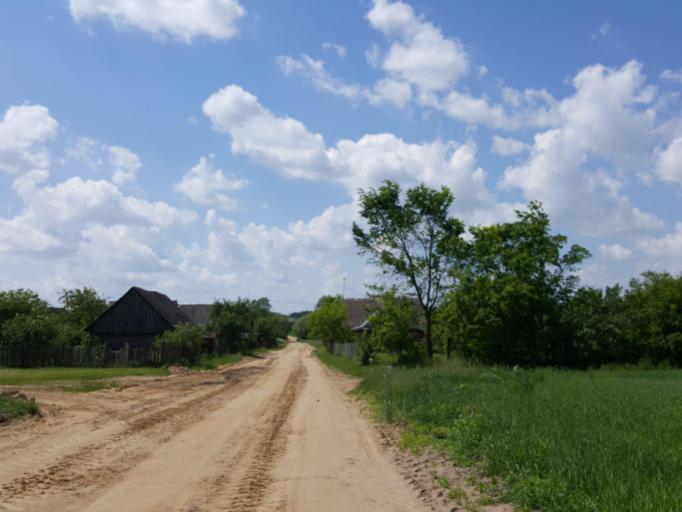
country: BY
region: Brest
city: Kamyanyets
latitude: 52.3982
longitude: 23.7594
